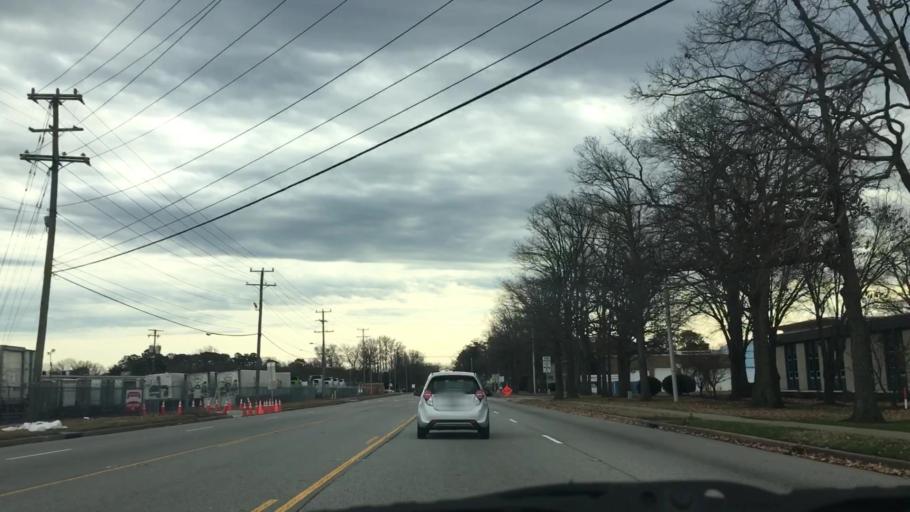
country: US
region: Virginia
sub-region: City of Norfolk
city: Norfolk
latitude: 36.8573
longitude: -76.2414
